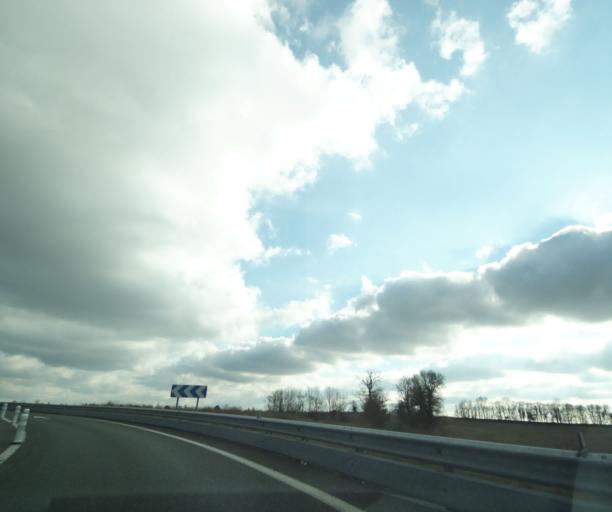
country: FR
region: Midi-Pyrenees
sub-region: Departement du Lot
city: Le Vigan
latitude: 44.6615
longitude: 1.5663
